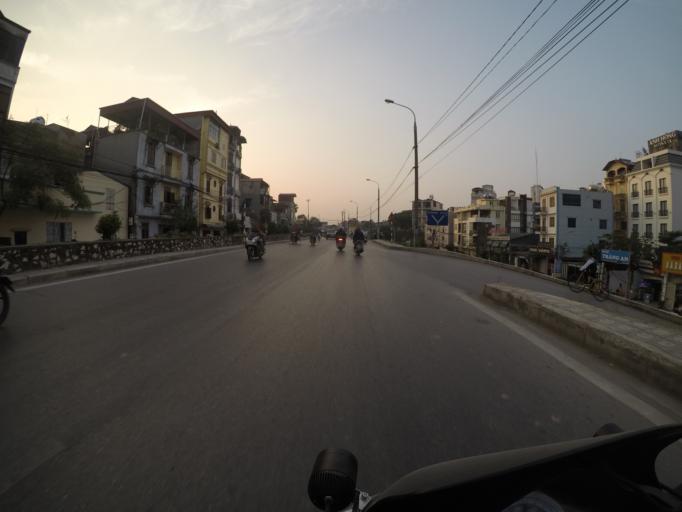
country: VN
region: Ha Noi
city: Hoan Kiem
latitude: 21.0388
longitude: 105.8674
